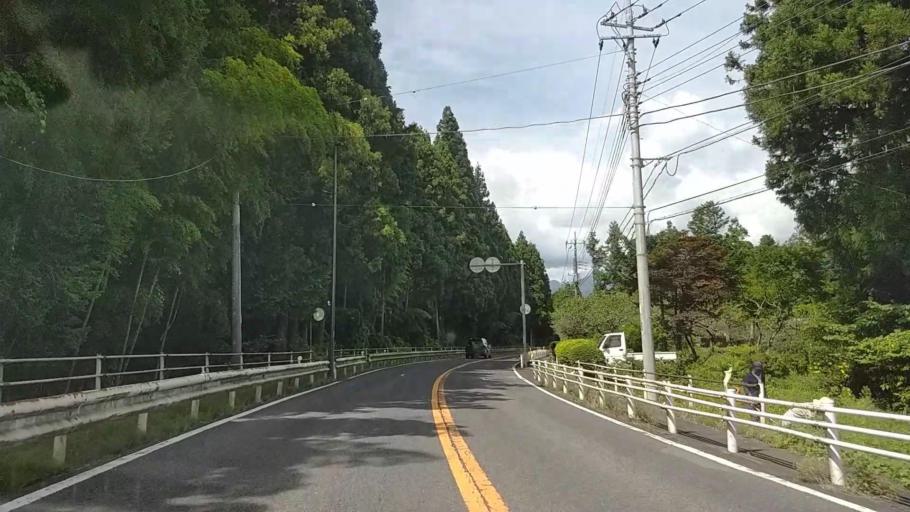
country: JP
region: Tochigi
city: Imaichi
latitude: 36.7284
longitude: 139.6707
